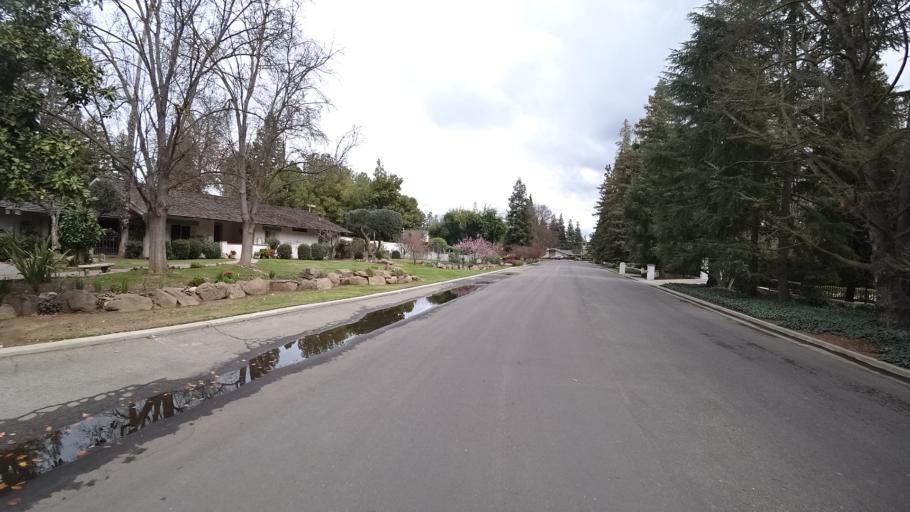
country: US
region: California
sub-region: Fresno County
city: Fresno
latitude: 36.8452
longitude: -119.8333
